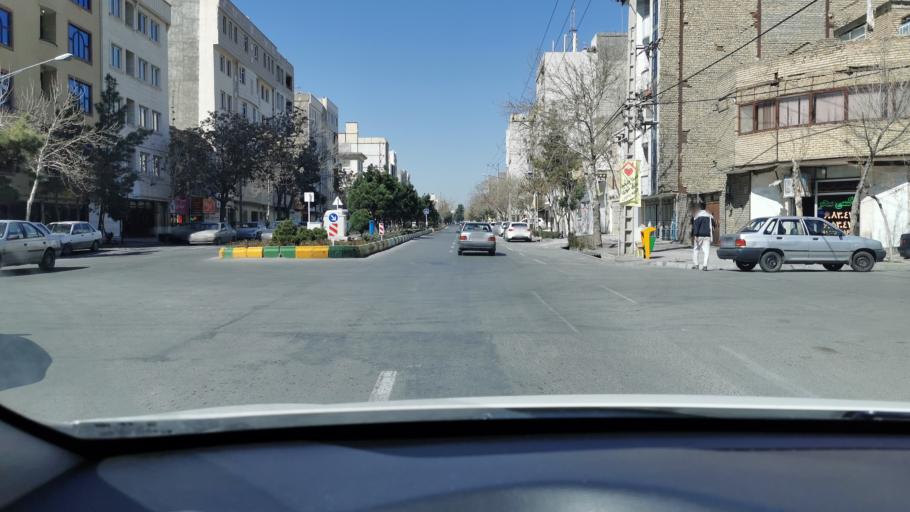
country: IR
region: Razavi Khorasan
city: Mashhad
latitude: 36.3254
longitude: 59.5235
